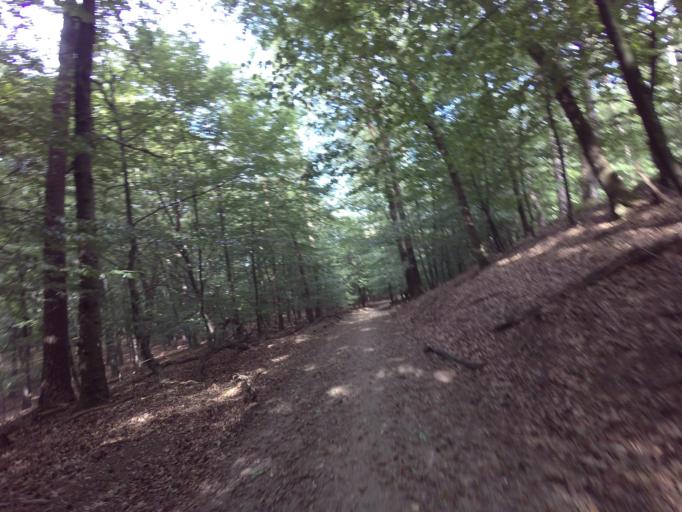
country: NL
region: Gelderland
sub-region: Gemeente Rheden
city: De Steeg
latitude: 52.0514
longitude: 6.0343
